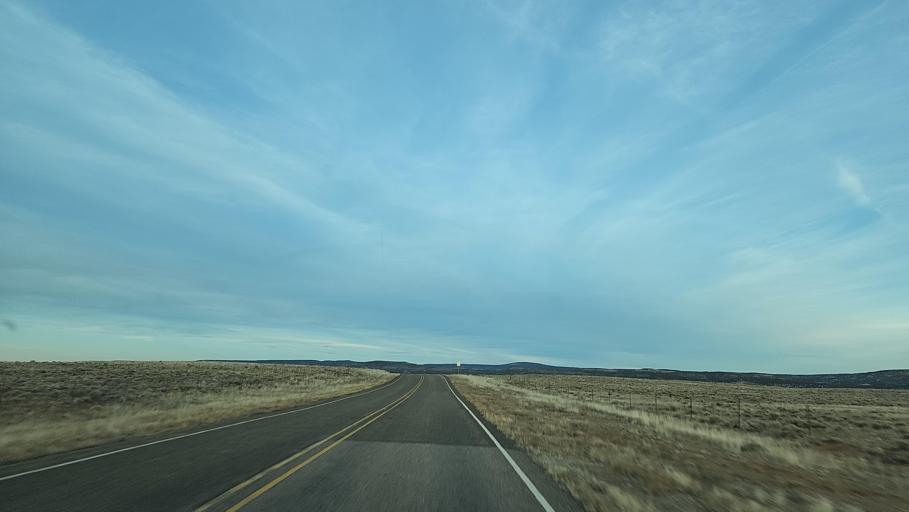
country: US
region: New Mexico
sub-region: Cibola County
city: Grants
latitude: 34.6985
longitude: -108.0430
